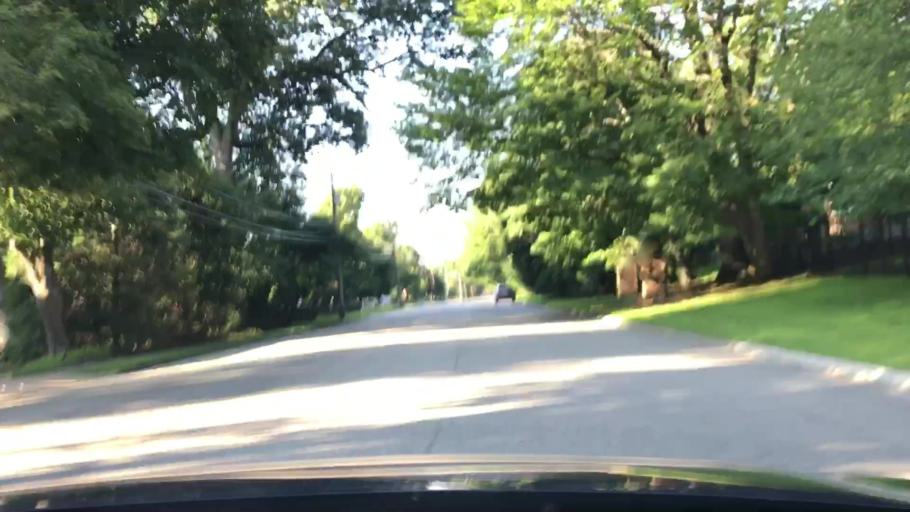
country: US
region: New Jersey
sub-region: Bergen County
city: Alpine
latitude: 40.9654
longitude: -73.9387
